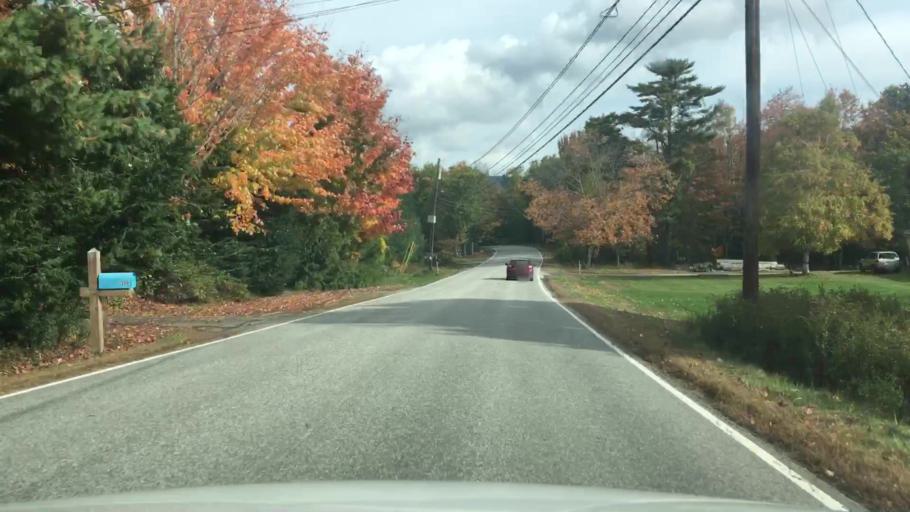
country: US
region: Maine
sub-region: Knox County
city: Rockport
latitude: 44.1877
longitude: -69.1111
